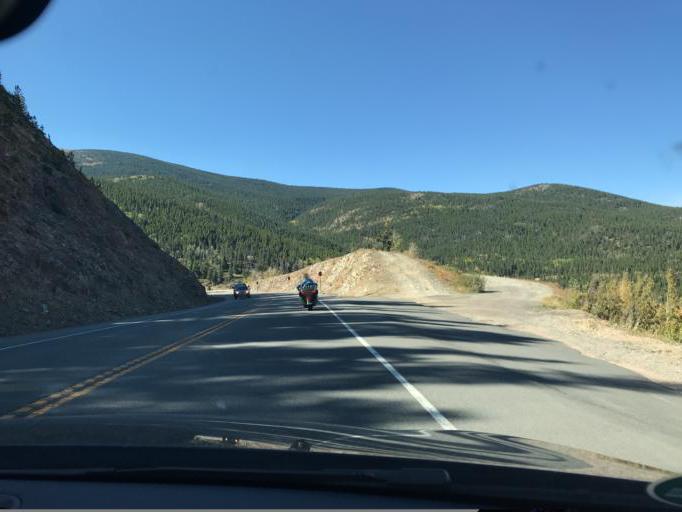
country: US
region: Colorado
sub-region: Boulder County
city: Nederland
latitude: 40.0527
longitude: -105.5194
